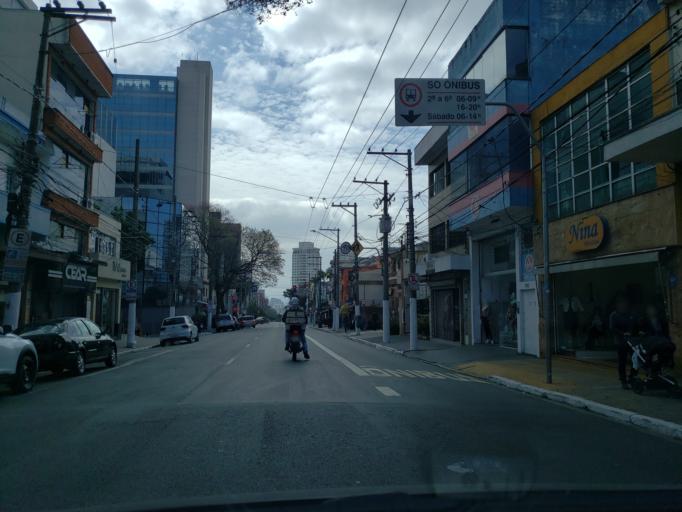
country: BR
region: Sao Paulo
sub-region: Sao Paulo
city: Sao Paulo
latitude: -23.5751
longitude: -46.6233
